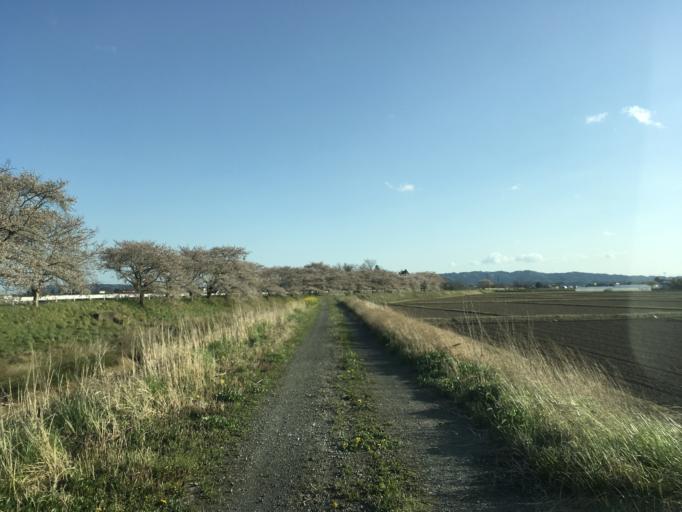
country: JP
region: Miyagi
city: Wakuya
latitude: 38.6540
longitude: 141.1459
